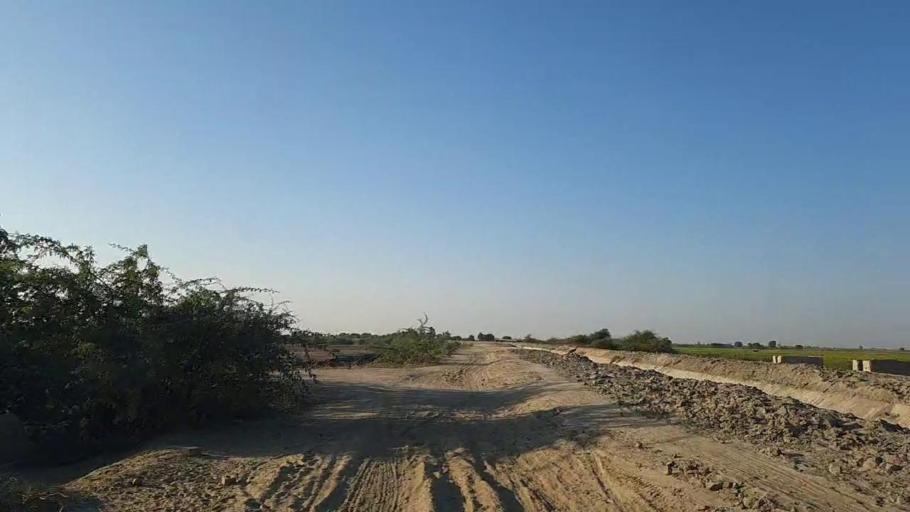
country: PK
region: Sindh
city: Naukot
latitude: 24.9990
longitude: 69.3985
